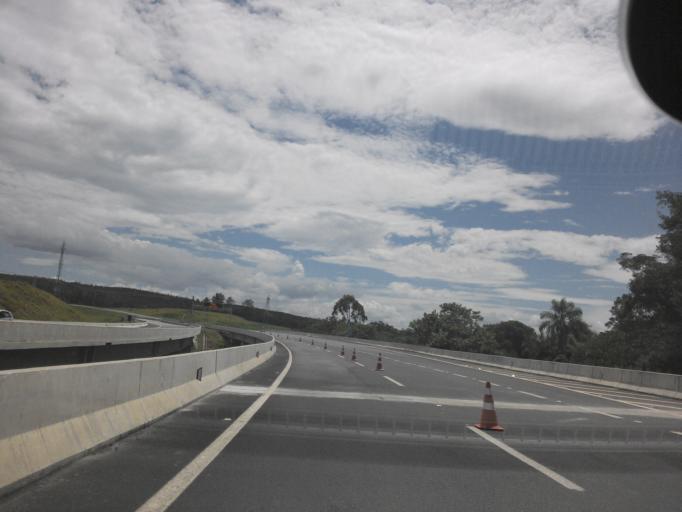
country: BR
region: Sao Paulo
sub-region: Taubate
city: Taubate
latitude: -23.0963
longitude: -45.6091
